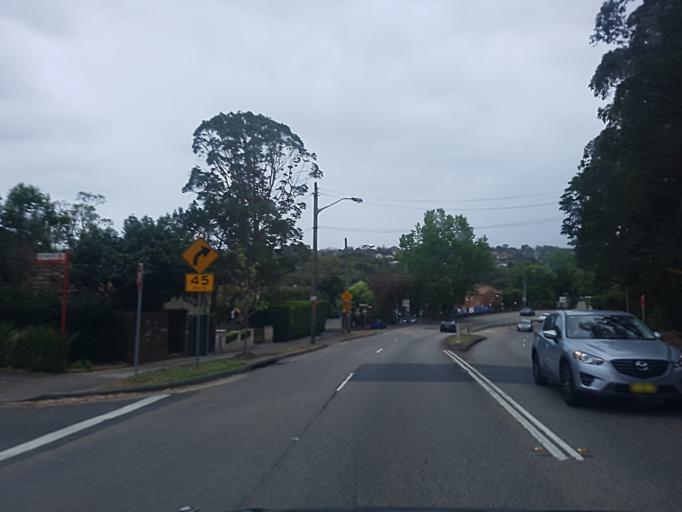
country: AU
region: New South Wales
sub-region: North Sydney
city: Cammeray
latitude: -33.8201
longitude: 151.2108
